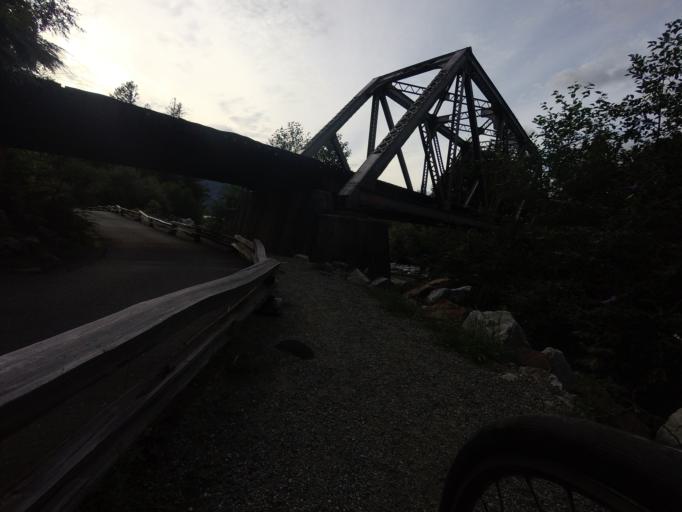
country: CA
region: British Columbia
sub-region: Greater Vancouver Regional District
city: Lions Bay
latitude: 49.5826
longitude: -123.2238
